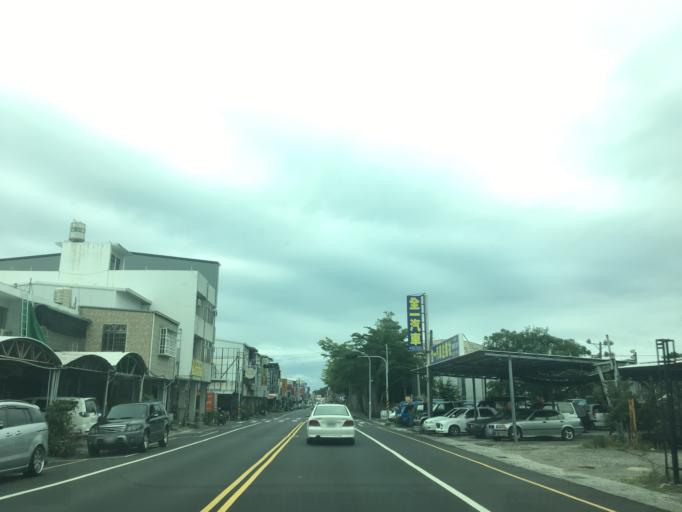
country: TW
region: Taiwan
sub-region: Taitung
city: Taitung
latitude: 22.7652
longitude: 121.1343
